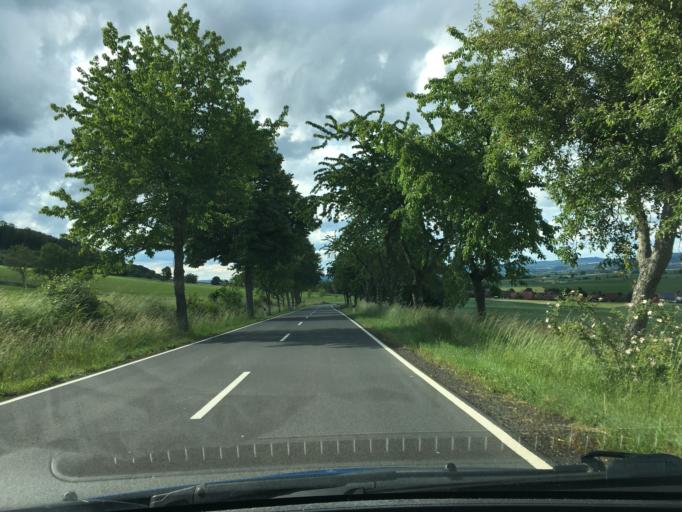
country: DE
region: Lower Saxony
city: Moringen
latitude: 51.7344
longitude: 9.8860
